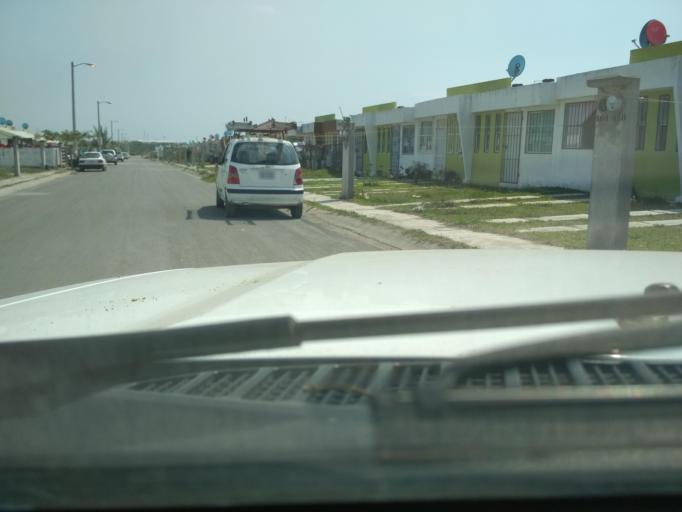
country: MX
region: Veracruz
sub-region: Veracruz
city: Lomas de Rio Medio Cuatro
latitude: 19.1877
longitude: -96.2112
